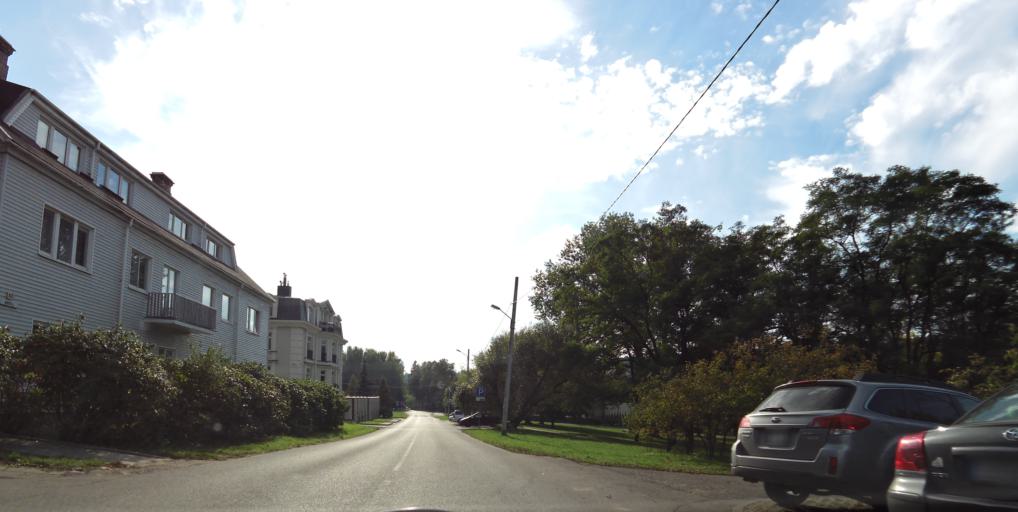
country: LT
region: Vilnius County
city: Seskine
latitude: 54.6912
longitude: 25.2463
